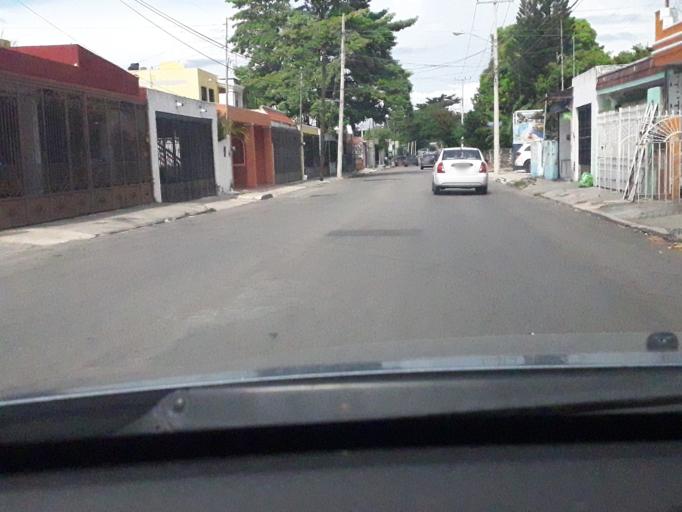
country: MX
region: Yucatan
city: Merida
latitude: 20.9789
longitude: -89.6553
